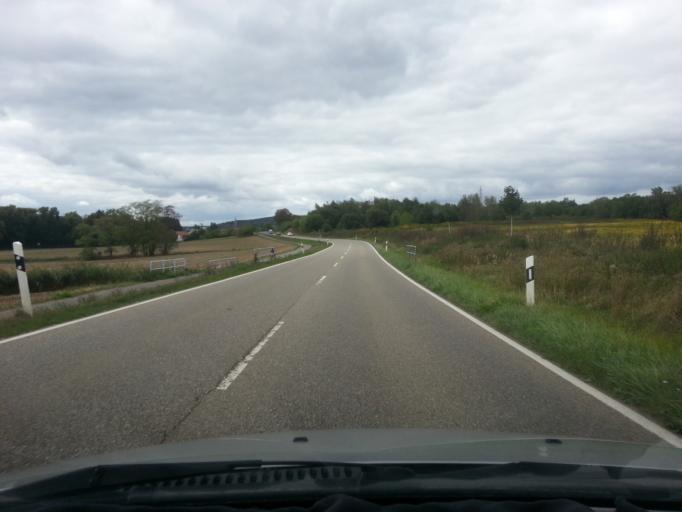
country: DE
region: Rheinland-Pfalz
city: Ebertsheim
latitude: 49.5652
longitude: 8.0954
